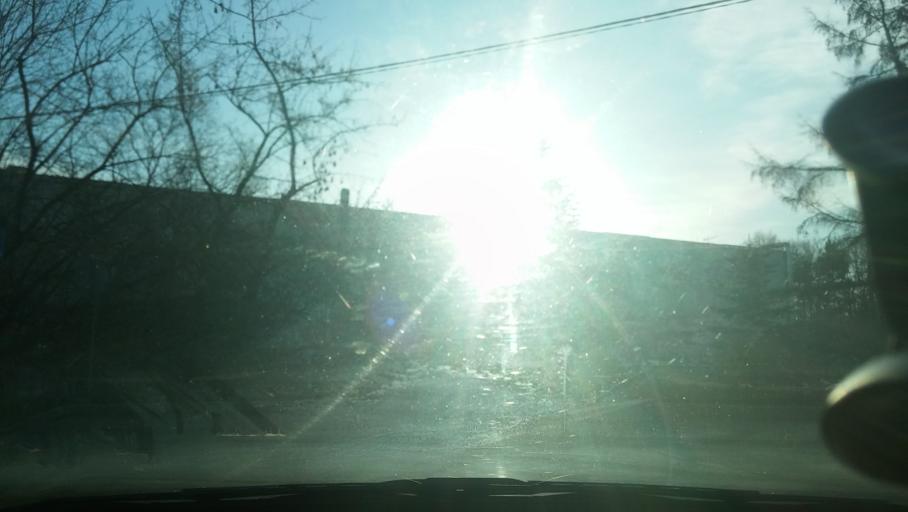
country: PL
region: Masovian Voivodeship
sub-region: Powiat piaseczynski
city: Piaseczno
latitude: 52.0657
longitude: 21.0196
